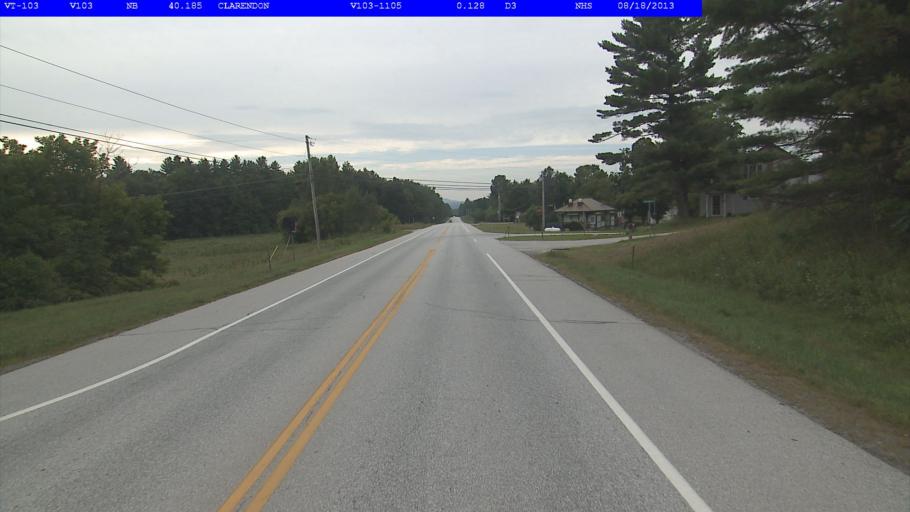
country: US
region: Vermont
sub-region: Rutland County
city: Rutland
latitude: 43.5252
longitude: -72.9324
